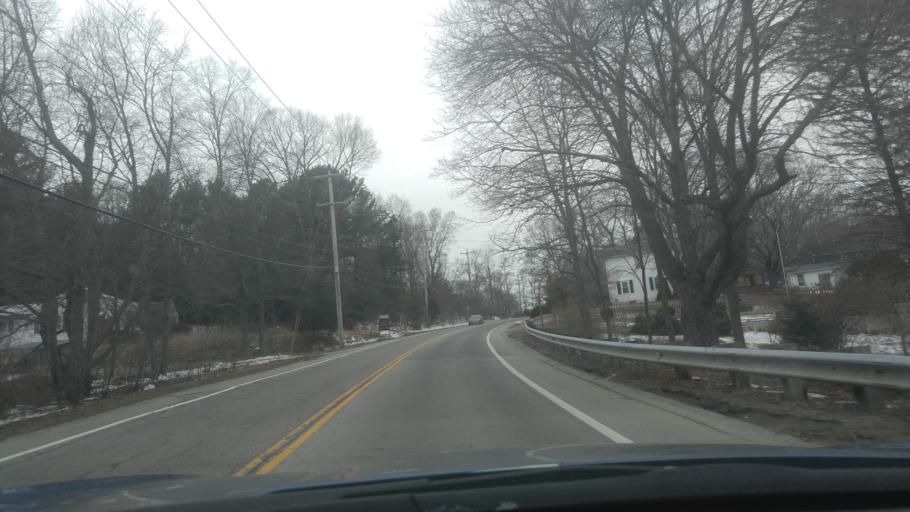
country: US
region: Rhode Island
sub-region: Kent County
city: West Warwick
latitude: 41.6798
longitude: -71.5393
